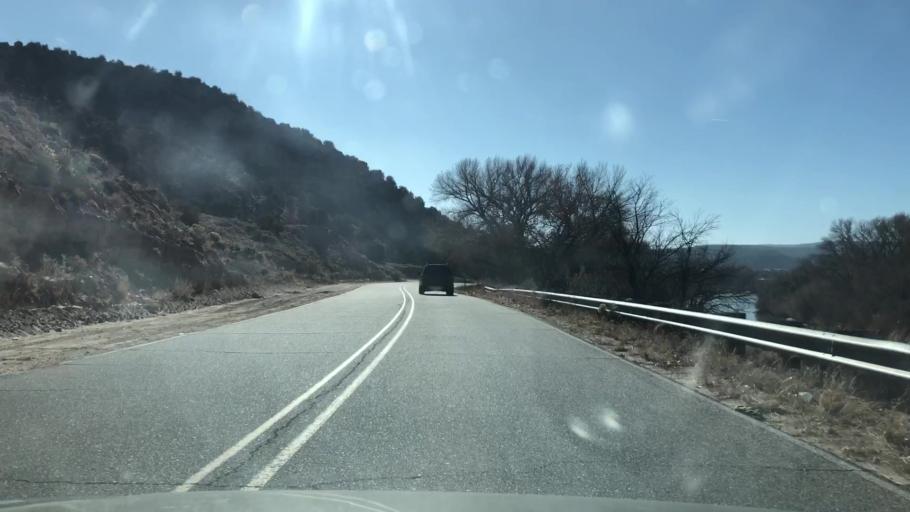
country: US
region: New Mexico
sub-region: Rio Arriba County
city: Ohkay Owingeh
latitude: 36.0921
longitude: -106.1296
